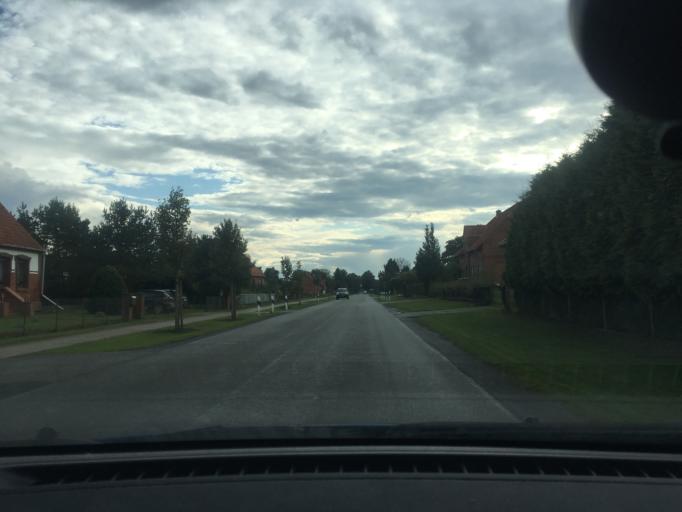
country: DE
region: Lower Saxony
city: Neu Darchau
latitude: 53.2649
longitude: 10.9206
